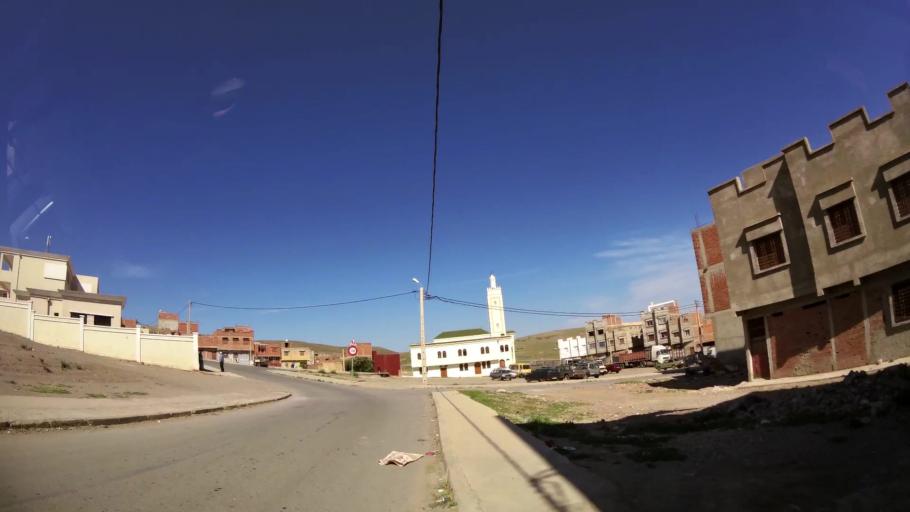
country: MA
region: Oriental
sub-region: Oujda-Angad
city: Oujda
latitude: 34.6473
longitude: -1.9458
